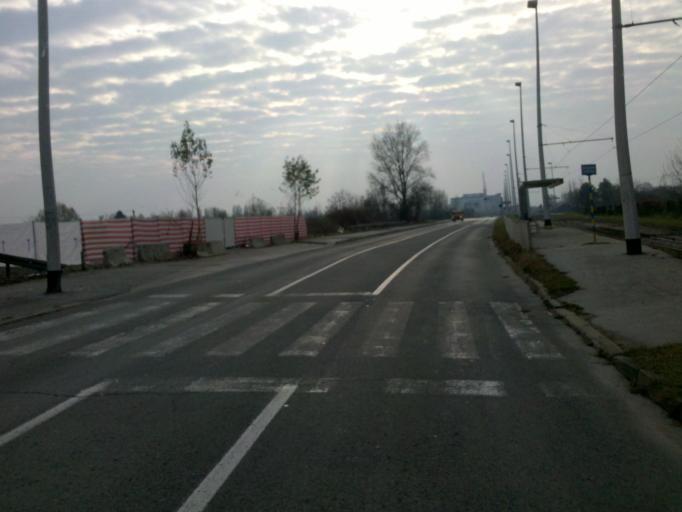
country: HR
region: Grad Zagreb
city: Dubrava
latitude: 45.7929
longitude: 16.0386
